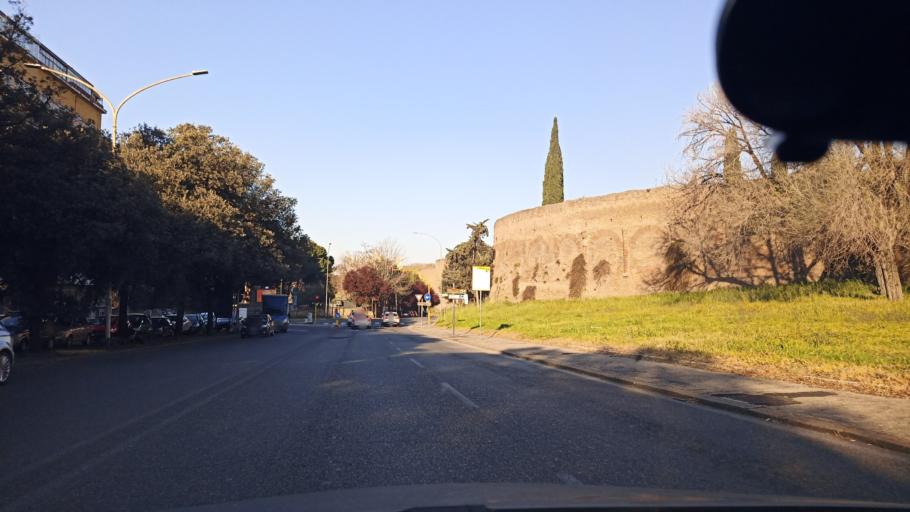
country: IT
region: Latium
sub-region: Citta metropolitana di Roma Capitale
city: Rome
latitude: 41.8873
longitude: 12.5162
